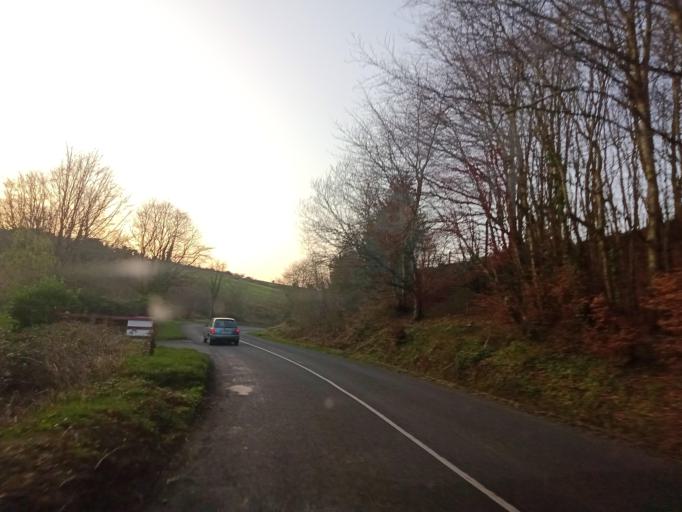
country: IE
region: Leinster
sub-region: Kilkenny
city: Castlecomer
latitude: 52.8413
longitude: -7.2575
